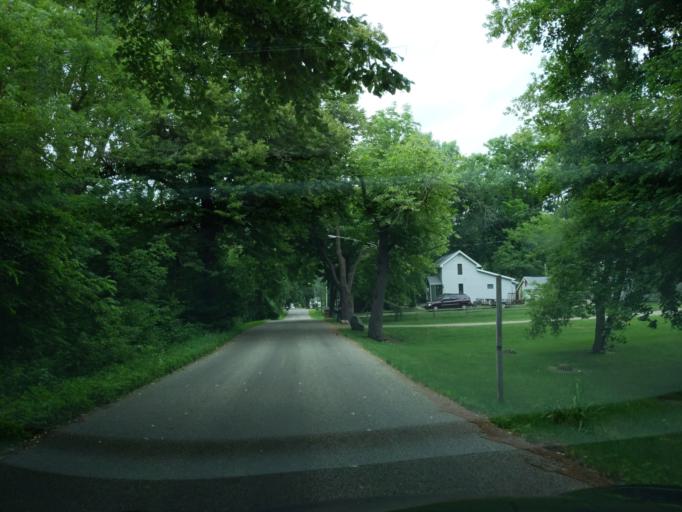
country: US
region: Michigan
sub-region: Ingham County
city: Lansing
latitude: 42.7710
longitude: -84.5600
